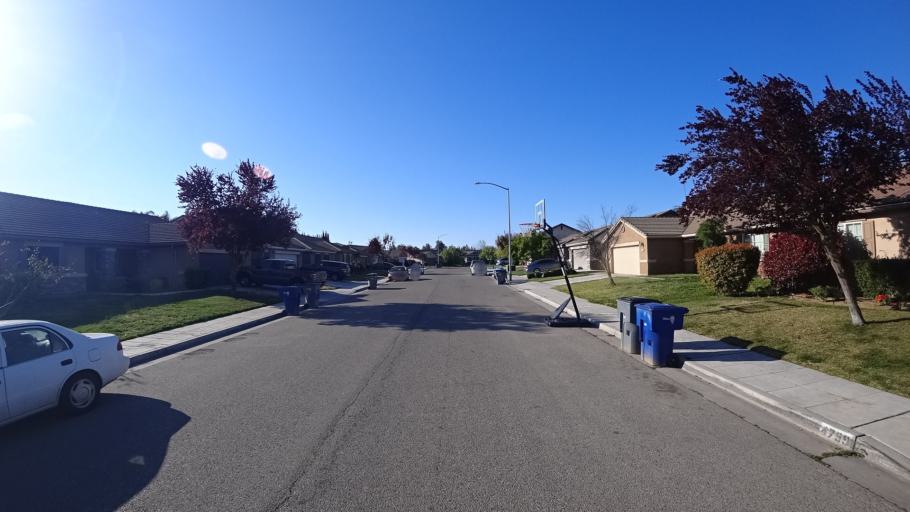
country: US
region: California
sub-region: Fresno County
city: Biola
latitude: 36.8048
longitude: -119.9116
